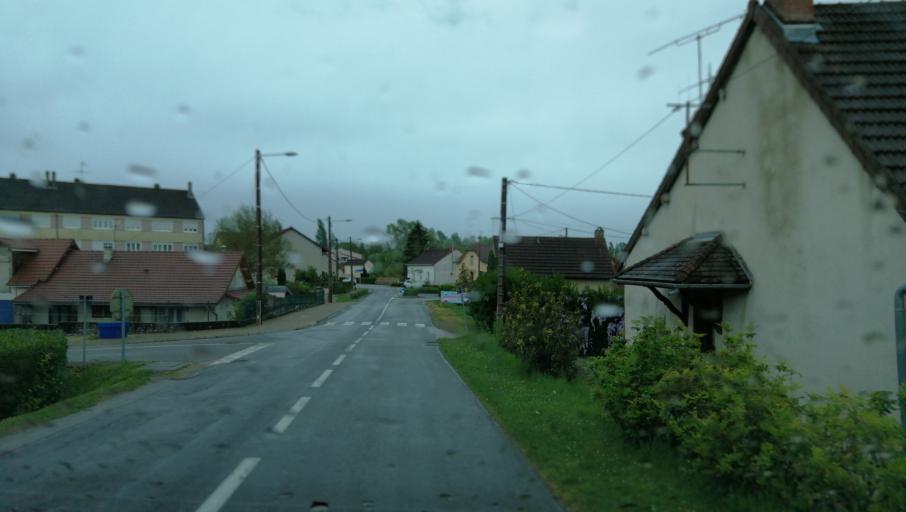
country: FR
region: Franche-Comte
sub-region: Departement du Jura
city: Bletterans
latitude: 46.7461
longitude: 5.4460
